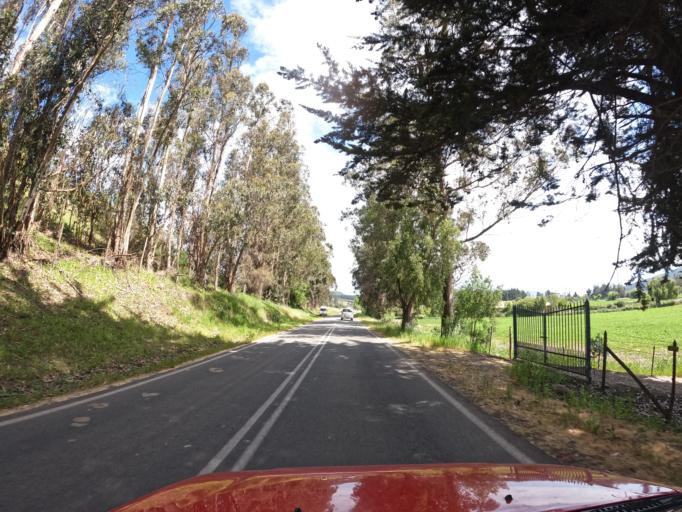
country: CL
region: Maule
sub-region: Provincia de Talca
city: Constitucion
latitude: -35.0112
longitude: -72.0363
